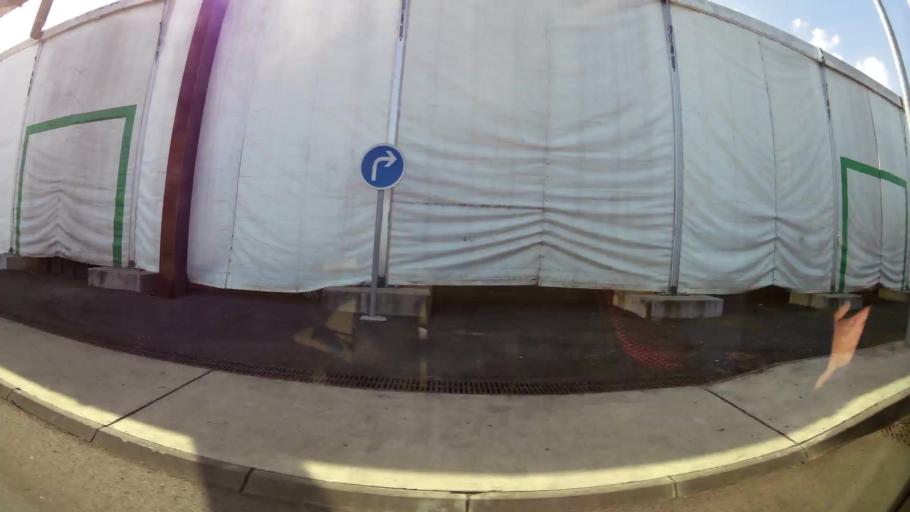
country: RE
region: Reunion
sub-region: Reunion
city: Le Tampon
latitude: -21.2842
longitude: 55.5129
